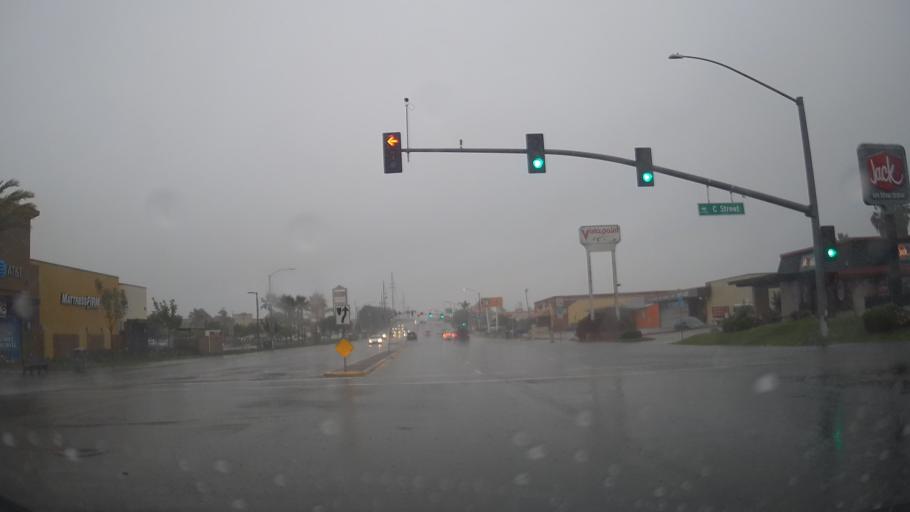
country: US
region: California
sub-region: San Diego County
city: Chula Vista
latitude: 32.6505
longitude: -117.0880
